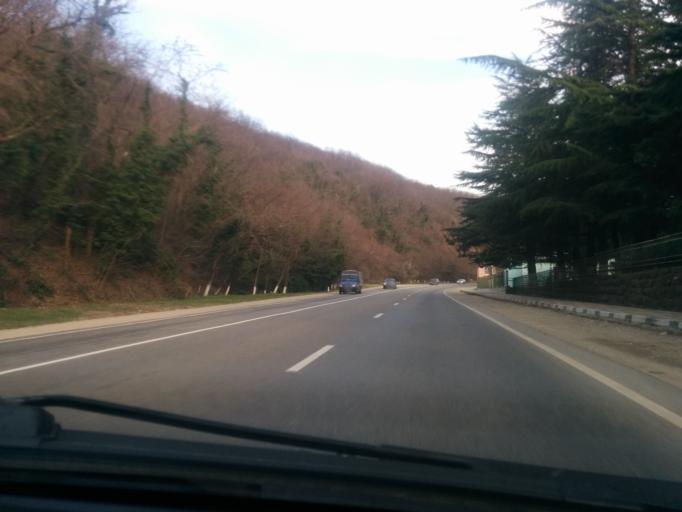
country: RU
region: Krasnodarskiy
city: Nebug
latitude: 44.1702
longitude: 38.9812
